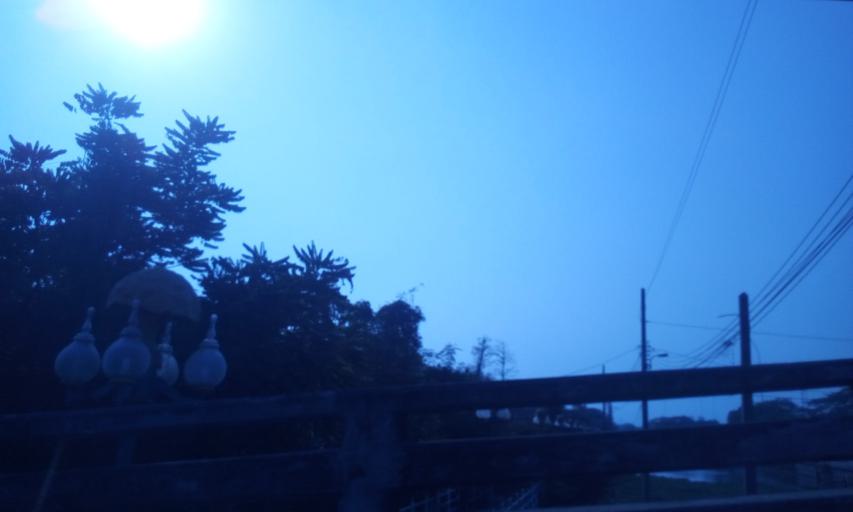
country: TH
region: Nonthaburi
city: Sai Noi
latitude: 13.9738
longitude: 100.3189
